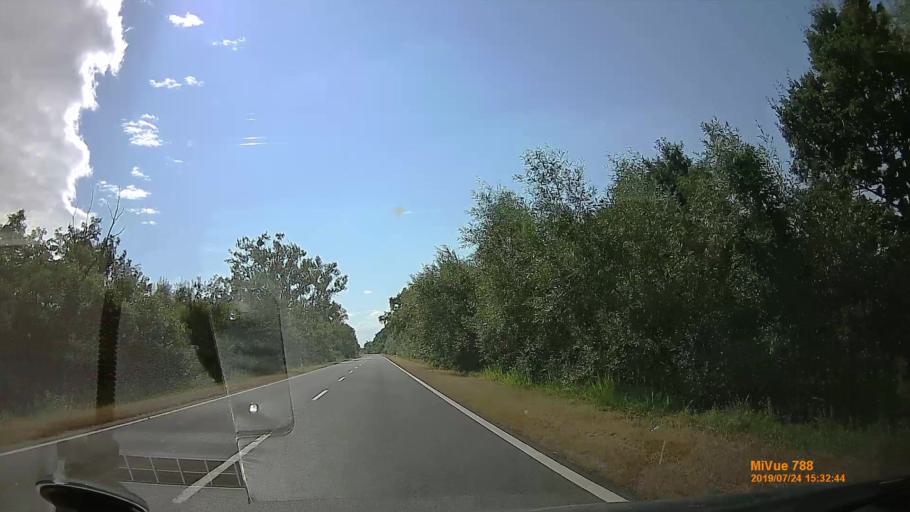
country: HU
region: Szabolcs-Szatmar-Bereg
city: Vasarosnameny
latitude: 48.1523
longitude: 22.4124
